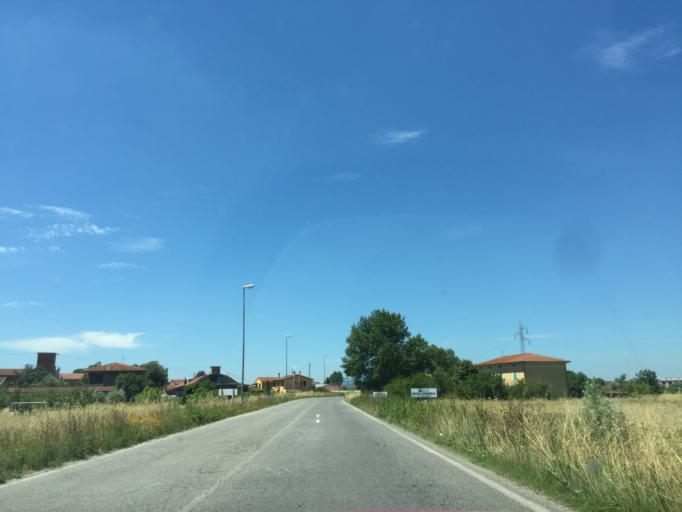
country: IT
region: Tuscany
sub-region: Province of Pisa
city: San Donato
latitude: 43.6899
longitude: 10.8043
